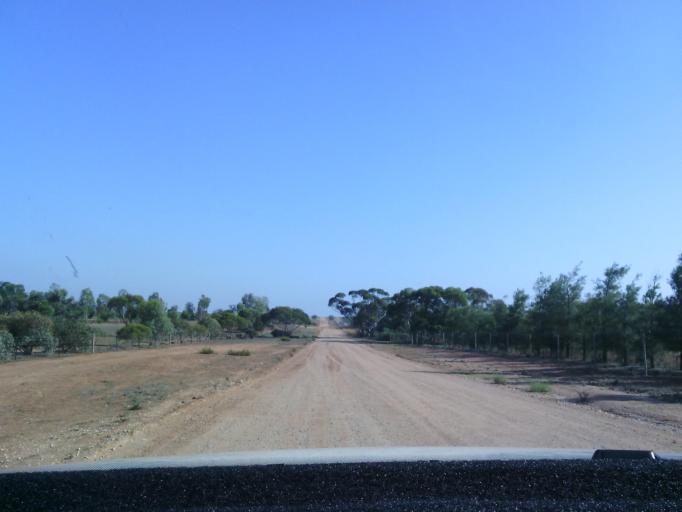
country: AU
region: South Australia
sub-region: Berri and Barmera
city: Monash
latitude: -34.2392
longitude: 140.5888
